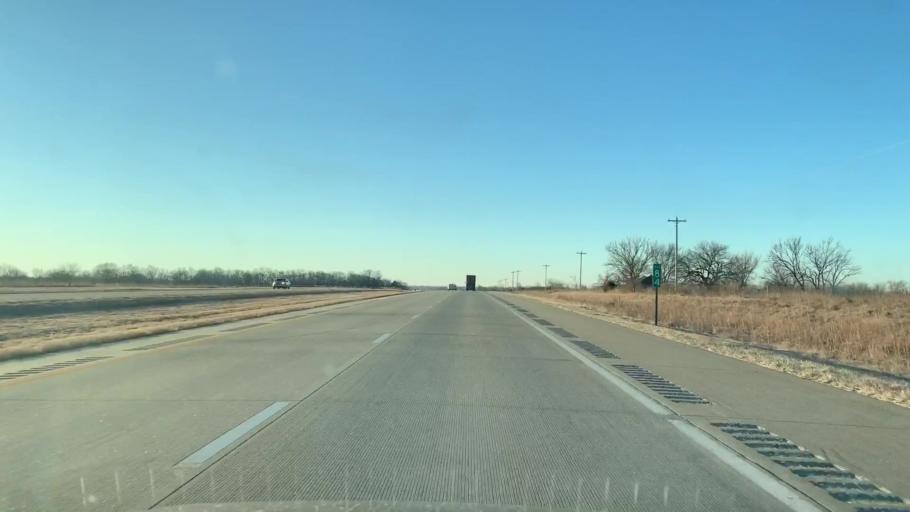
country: US
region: Kansas
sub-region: Linn County
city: Pleasanton
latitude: 38.0932
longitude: -94.7137
